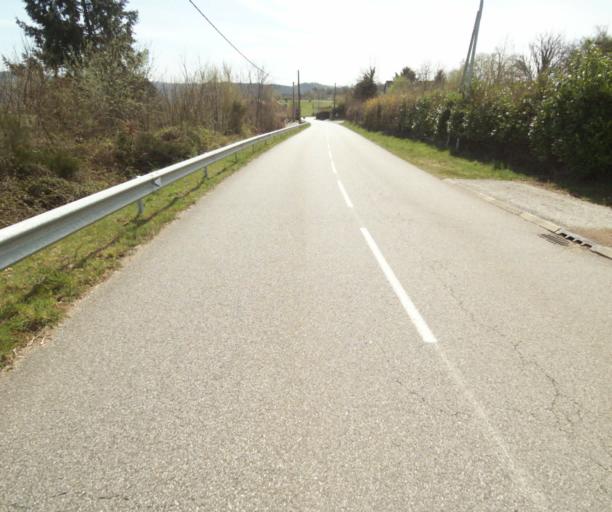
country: FR
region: Limousin
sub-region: Departement de la Correze
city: Naves
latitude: 45.3600
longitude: 1.7969
